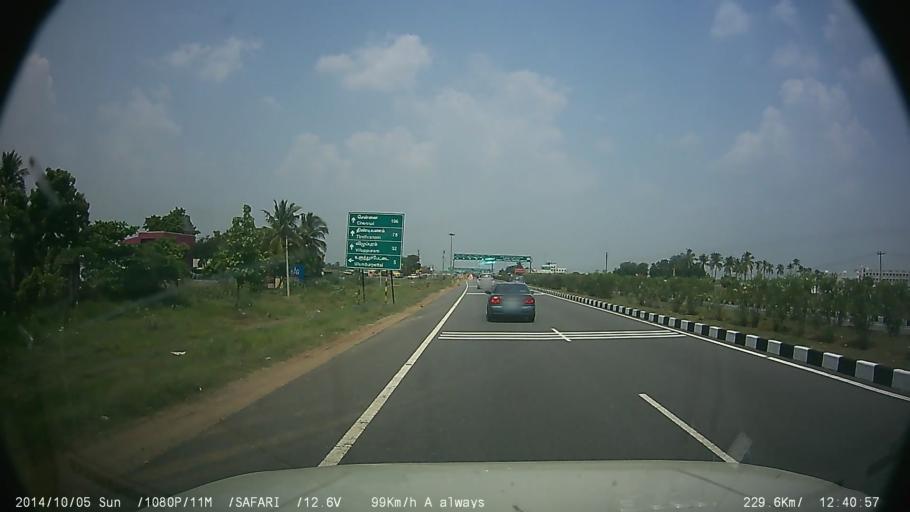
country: IN
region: Tamil Nadu
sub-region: Cuddalore
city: Vriddhachalam
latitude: 11.7010
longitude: 79.3190
